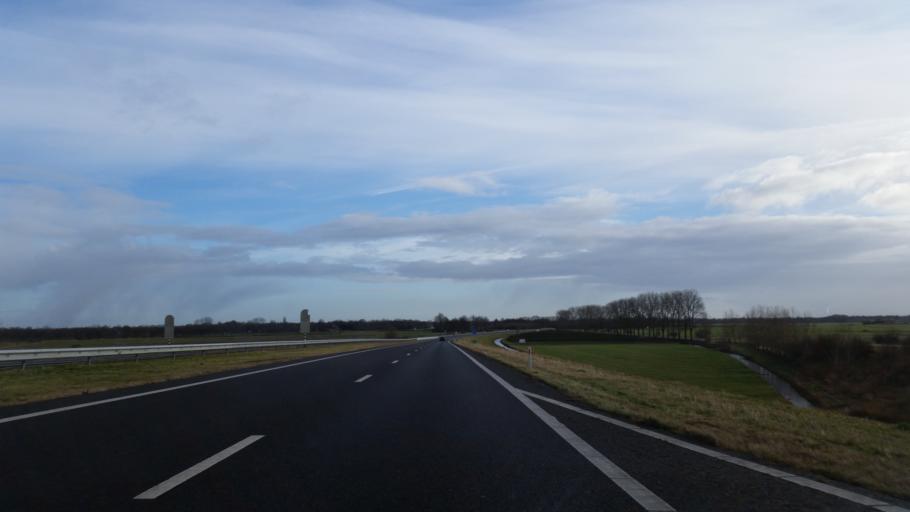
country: NL
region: Friesland
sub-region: Gemeente Tytsjerksteradiel
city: Garyp
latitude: 53.1639
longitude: 5.9360
